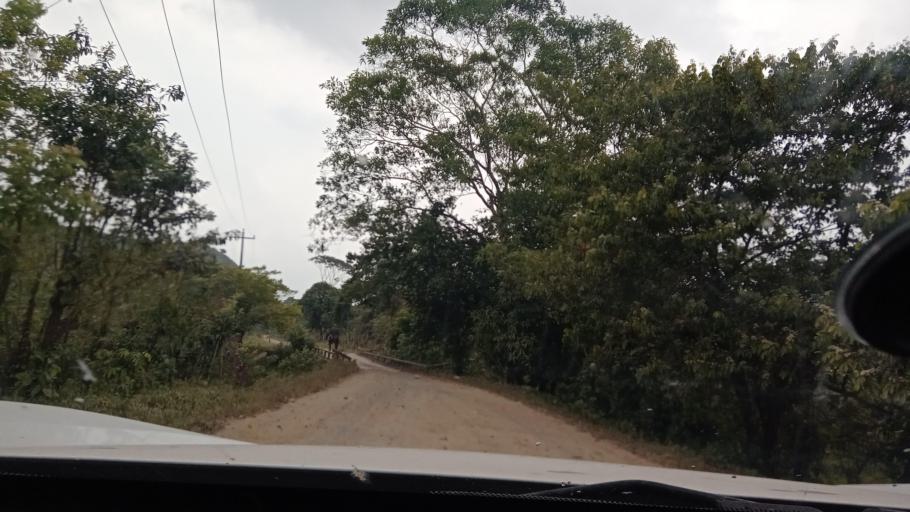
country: MX
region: Veracruz
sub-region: Uxpanapa
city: Poblado 10
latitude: 17.4559
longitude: -94.0943
